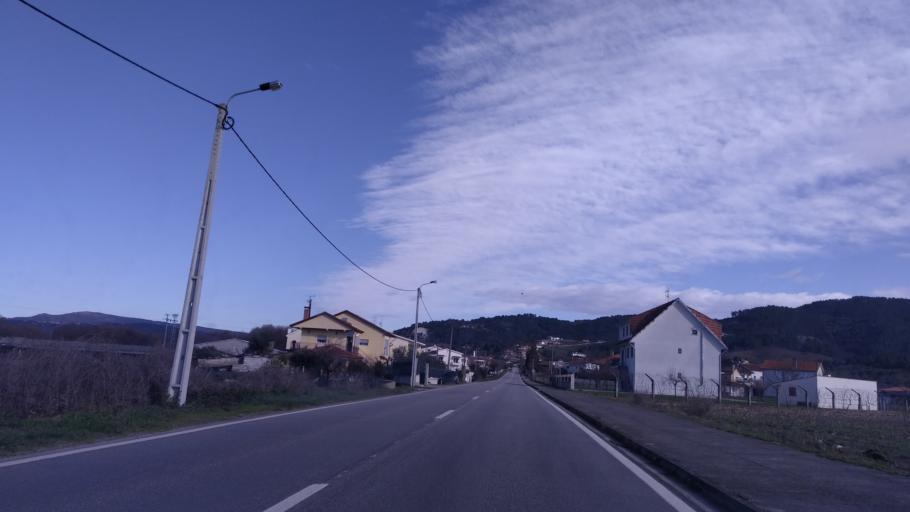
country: PT
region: Vila Real
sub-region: Chaves
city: Chaves
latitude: 41.7445
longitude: -7.4419
